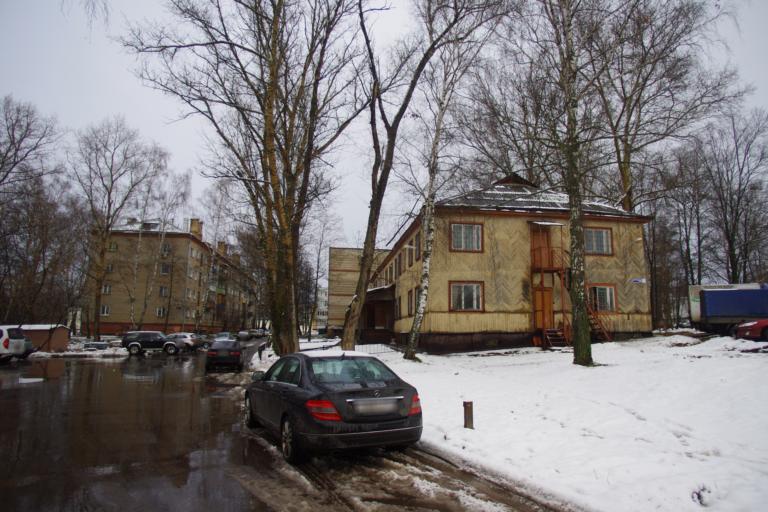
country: RU
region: Moskovskaya
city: Krasnogorsk
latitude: 55.8081
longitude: 37.3147
